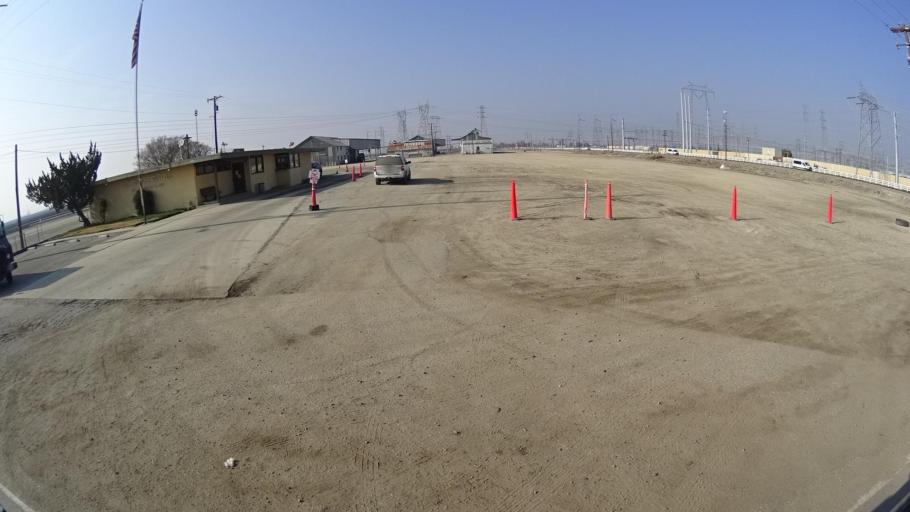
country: US
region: California
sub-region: Kern County
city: Buttonwillow
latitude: 35.3985
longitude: -119.4476
